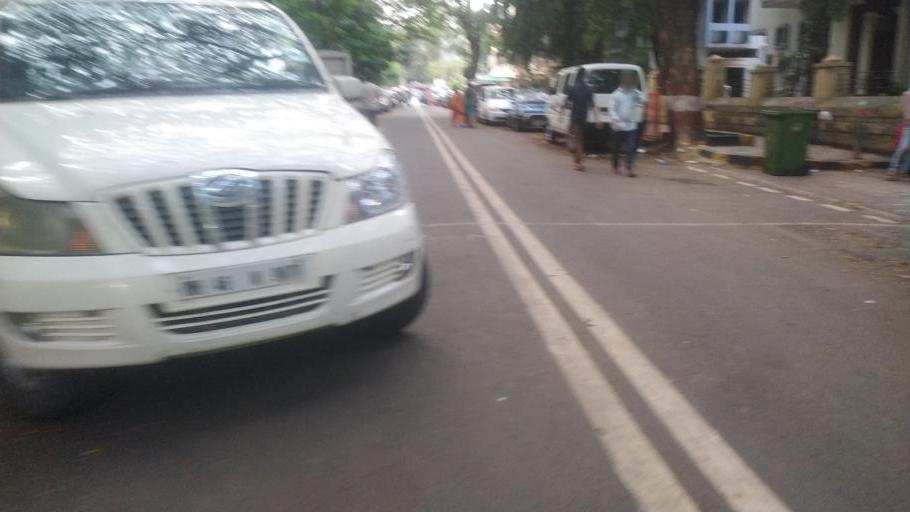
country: IN
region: Maharashtra
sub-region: Mumbai Suburban
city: Mumbai
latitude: 19.0172
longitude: 72.8570
